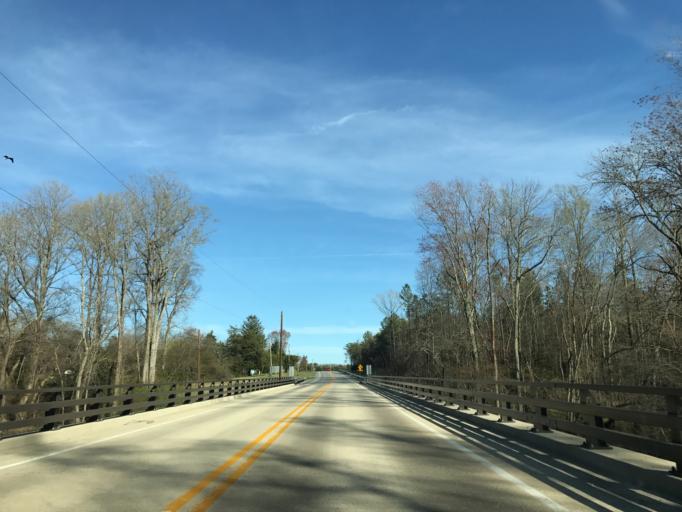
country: US
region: Maryland
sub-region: Caroline County
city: Greensboro
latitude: 39.0304
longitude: -75.7582
